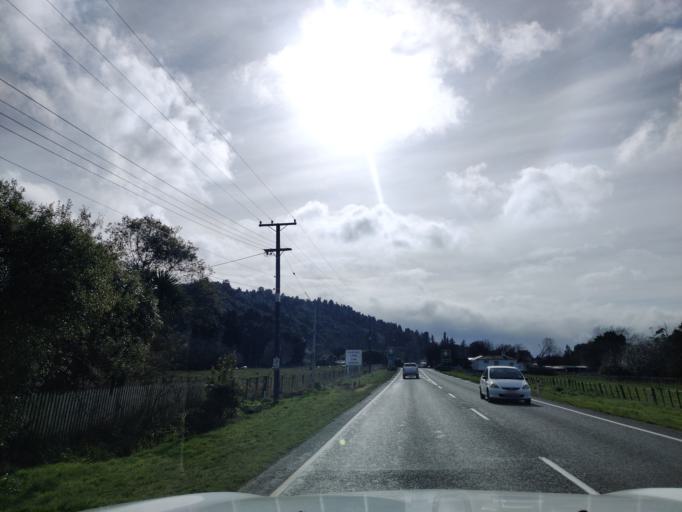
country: NZ
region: Manawatu-Wanganui
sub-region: Ruapehu District
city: Waiouru
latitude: -39.8129
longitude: 175.7844
